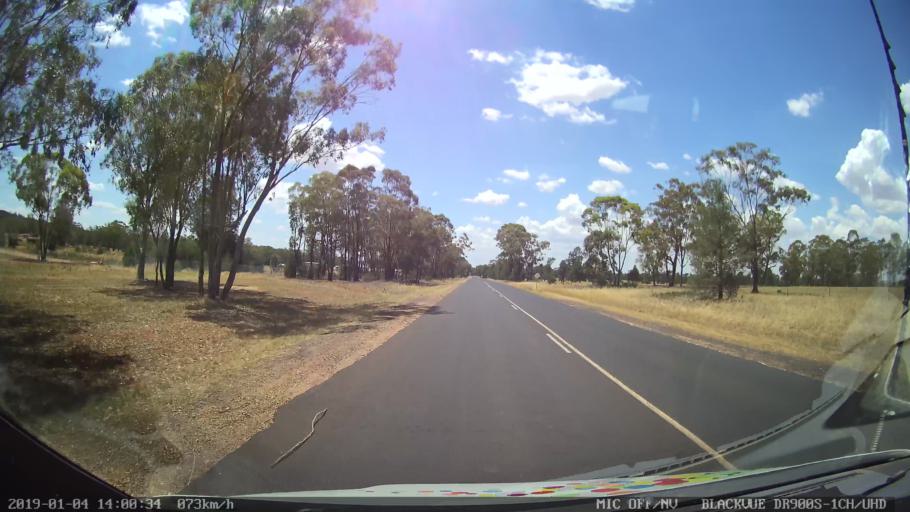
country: AU
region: New South Wales
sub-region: Dubbo Municipality
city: Dubbo
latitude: -32.3055
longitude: 148.5940
